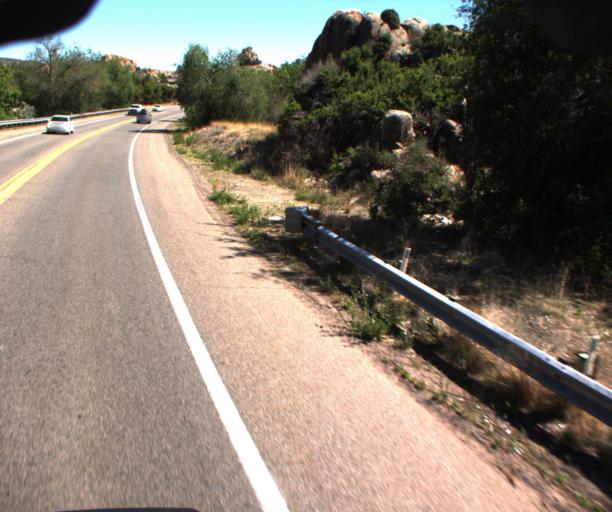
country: US
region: Arizona
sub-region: Yavapai County
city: Prescott
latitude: 34.6152
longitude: -112.4197
